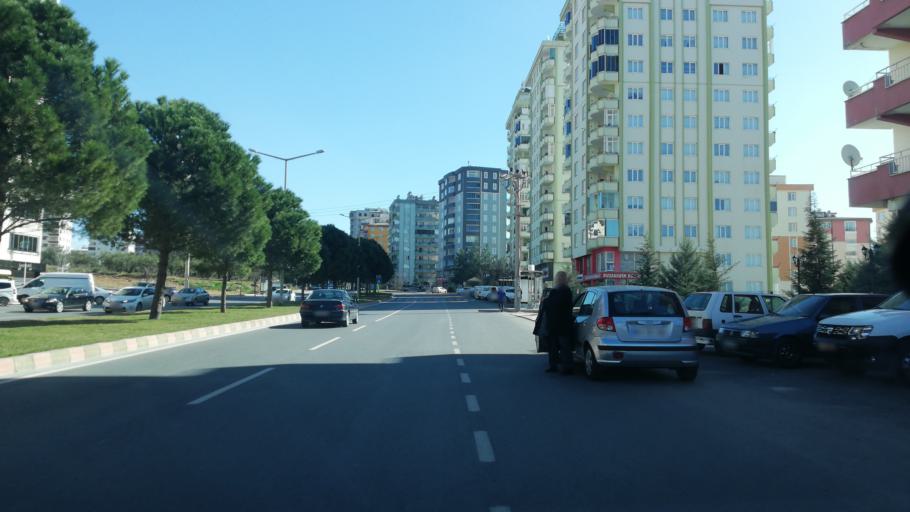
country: TR
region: Kahramanmaras
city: Kahramanmaras
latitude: 37.5830
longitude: 36.8800
